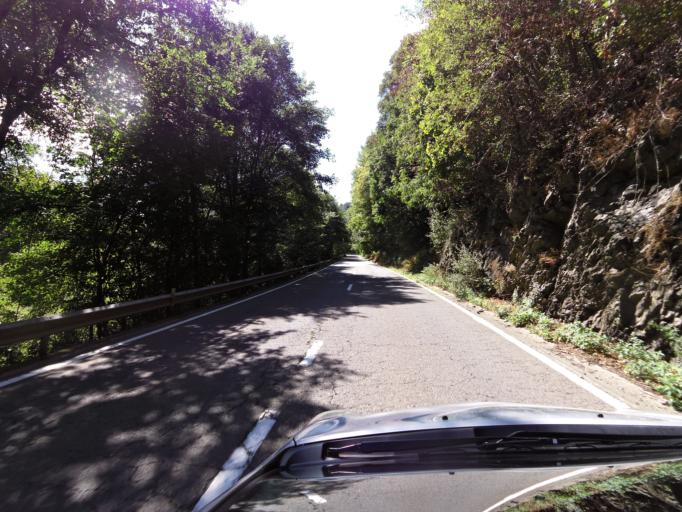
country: BE
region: Wallonia
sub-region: Province du Luxembourg
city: Rendeux
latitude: 50.2207
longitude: 5.5204
